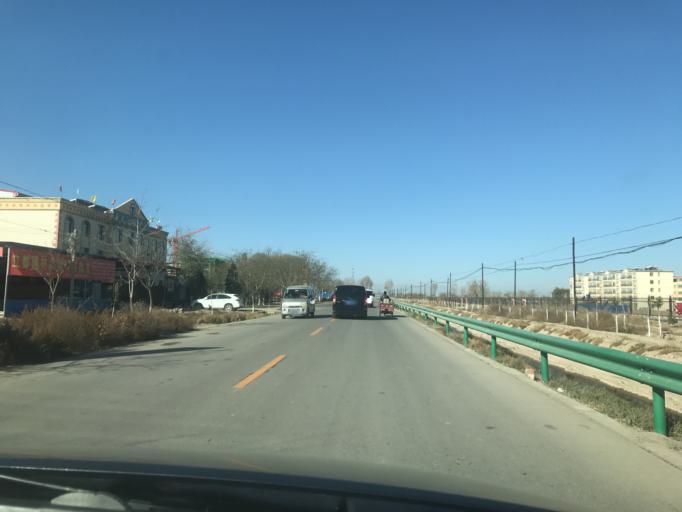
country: CN
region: Gansu Sheng
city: Gulang
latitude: 37.6753
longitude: 102.8416
